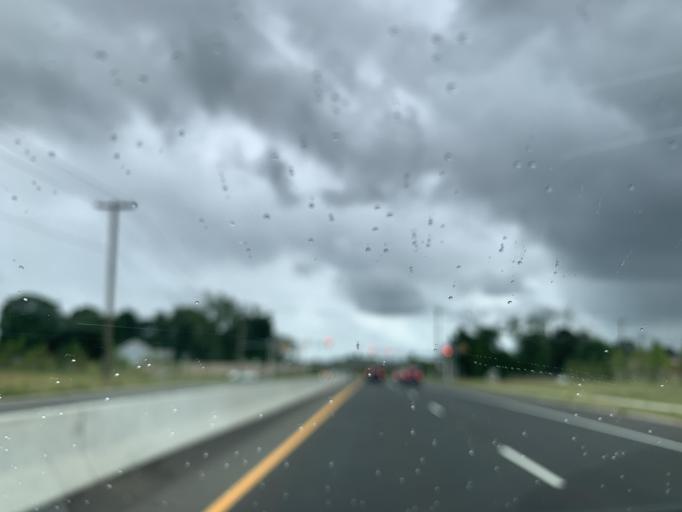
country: US
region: New Jersey
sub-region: Somerset County
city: Bloomingdale
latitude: 40.5096
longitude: -74.6335
